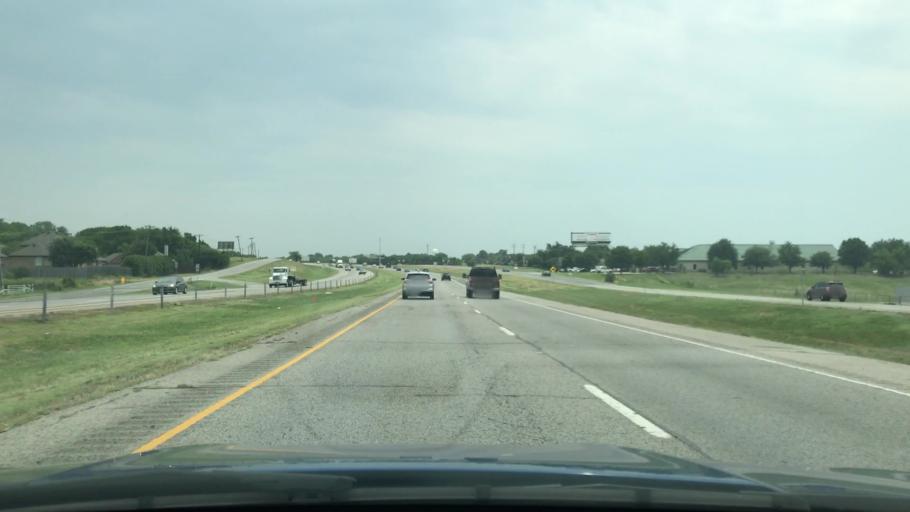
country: US
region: Texas
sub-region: Kaufman County
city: Forney
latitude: 32.7638
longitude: -96.4830
